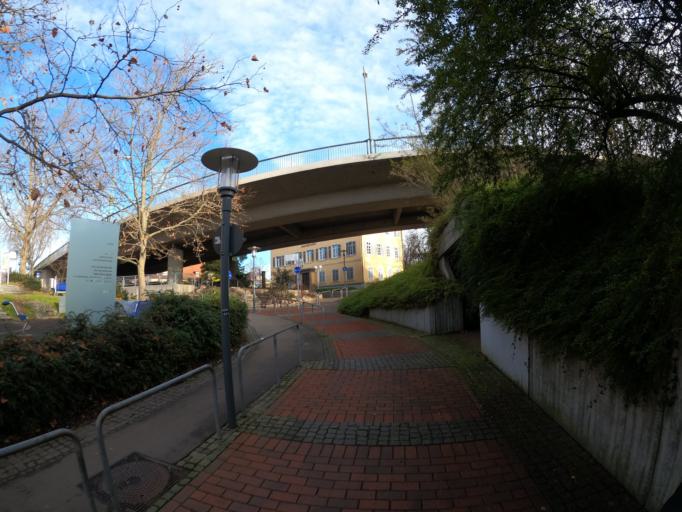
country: DE
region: Baden-Wuerttemberg
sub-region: Regierungsbezirk Stuttgart
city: Eislingen
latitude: 48.6978
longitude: 9.7058
